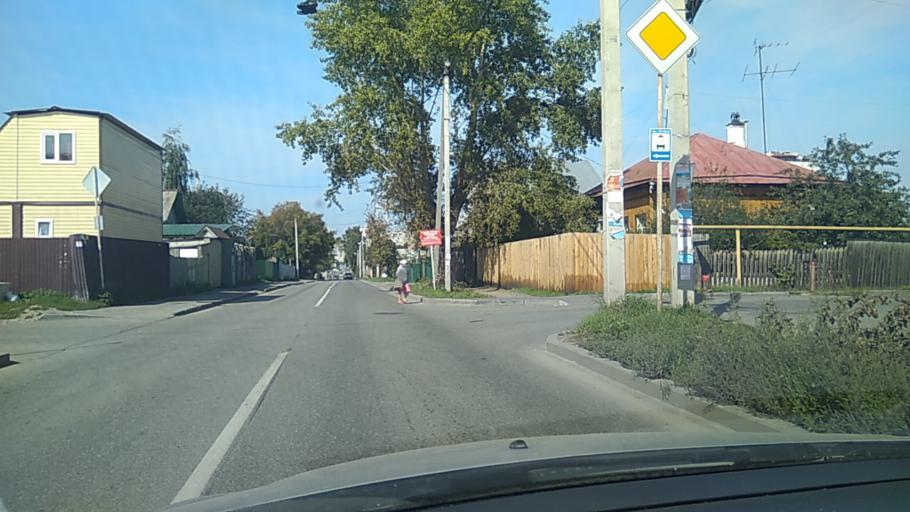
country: RU
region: Sverdlovsk
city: Sovkhoznyy
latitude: 56.8077
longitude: 60.5701
